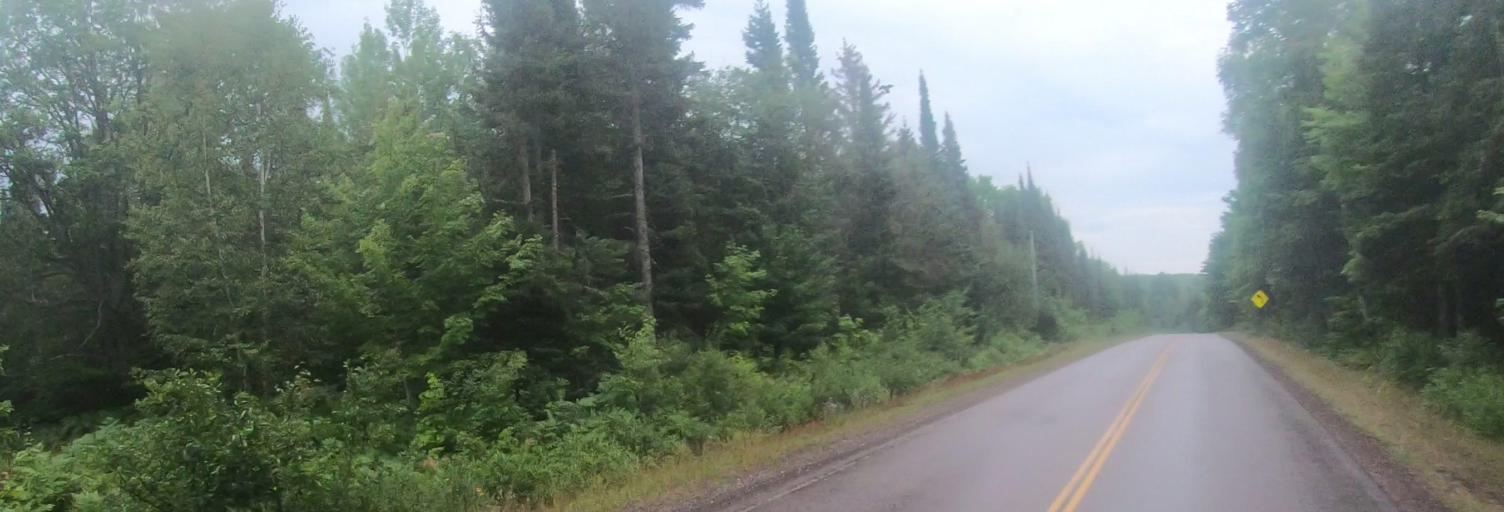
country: US
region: Michigan
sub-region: Keweenaw County
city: Eagle River
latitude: 47.2904
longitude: -88.3233
